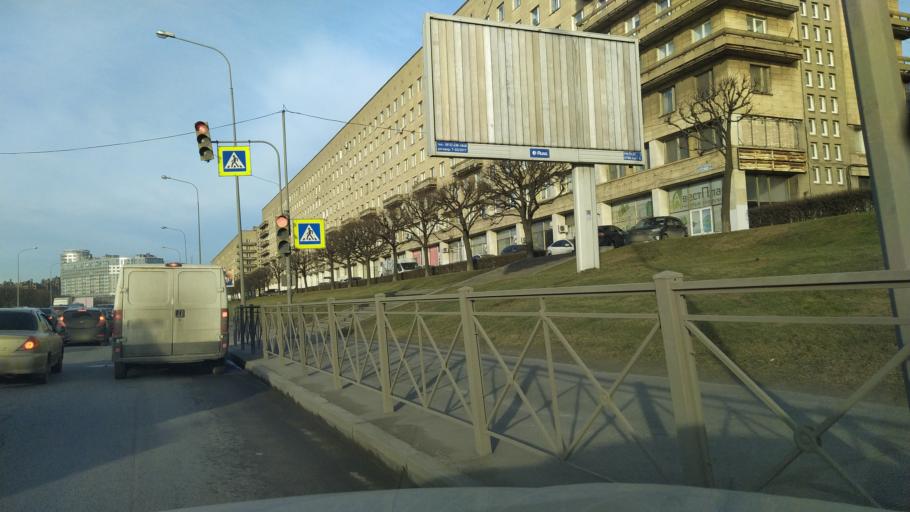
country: RU
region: Leningrad
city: Finlyandskiy
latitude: 59.9490
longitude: 30.4073
